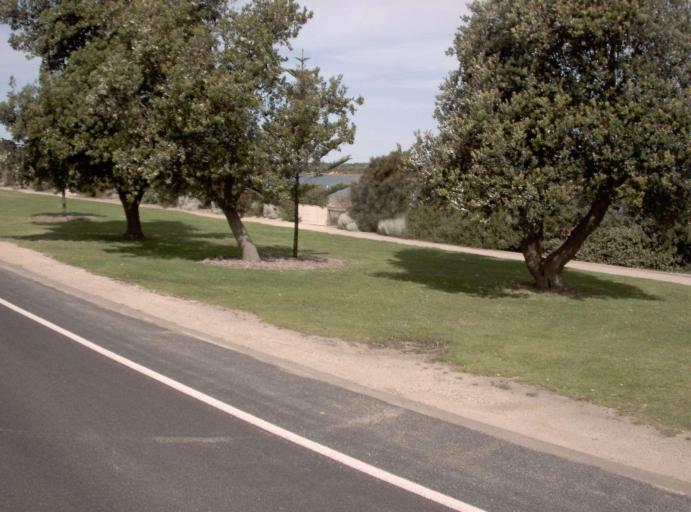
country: AU
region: Victoria
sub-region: East Gippsland
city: Lakes Entrance
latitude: -37.8783
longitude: 147.9971
